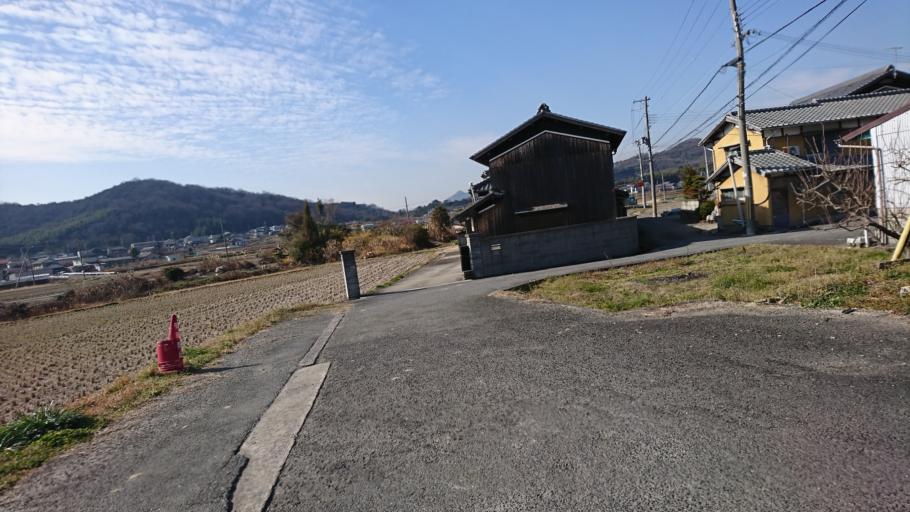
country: JP
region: Hyogo
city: Kakogawacho-honmachi
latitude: 34.8150
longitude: 134.8556
